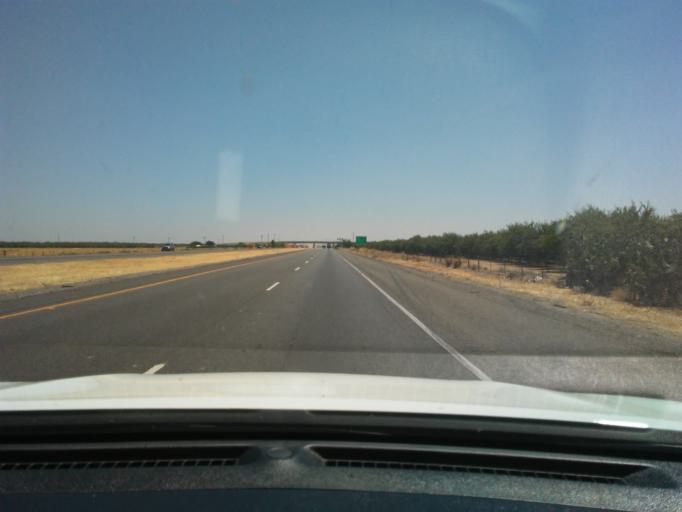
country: US
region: California
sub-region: Merced County
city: Gustine
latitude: 37.1374
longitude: -121.0373
